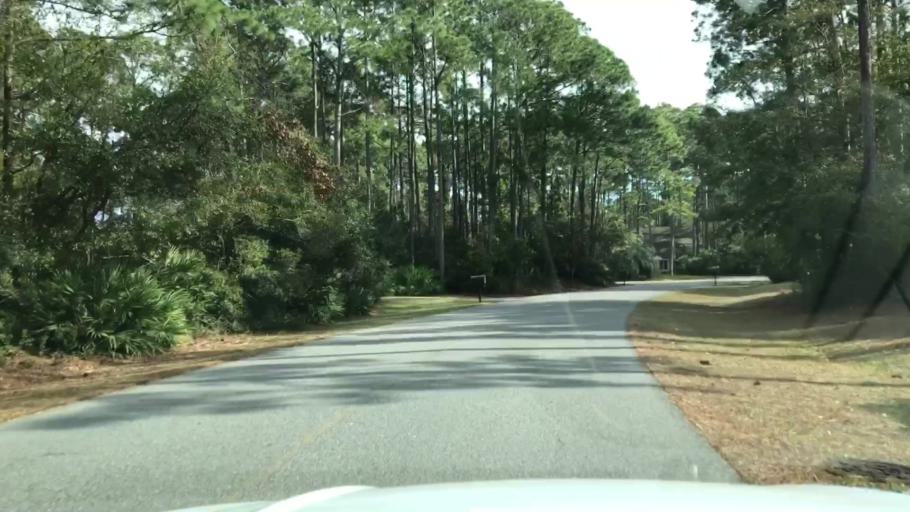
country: US
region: South Carolina
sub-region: Beaufort County
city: Hilton Head Island
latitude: 32.2450
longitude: -80.7077
